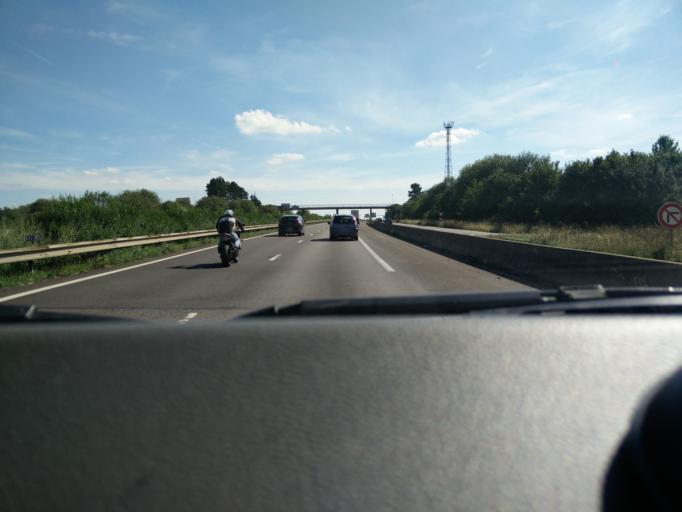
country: FR
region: Lorraine
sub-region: Departement de la Moselle
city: Illange
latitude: 49.3323
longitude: 6.1855
